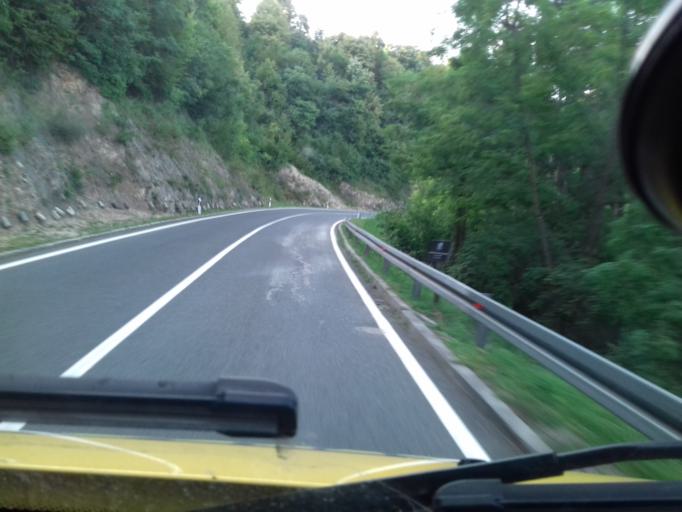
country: BA
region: Federation of Bosnia and Herzegovina
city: Ostrozac
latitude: 44.9013
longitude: 15.9306
